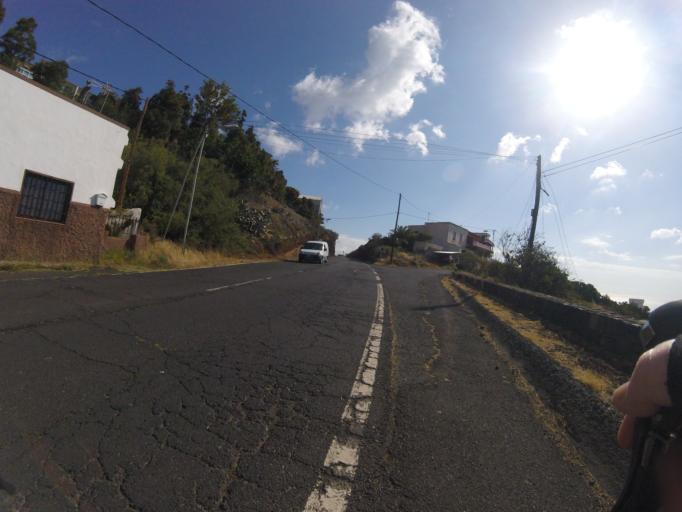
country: ES
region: Canary Islands
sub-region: Provincia de Santa Cruz de Tenerife
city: La Laguna
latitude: 28.4164
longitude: -16.3216
